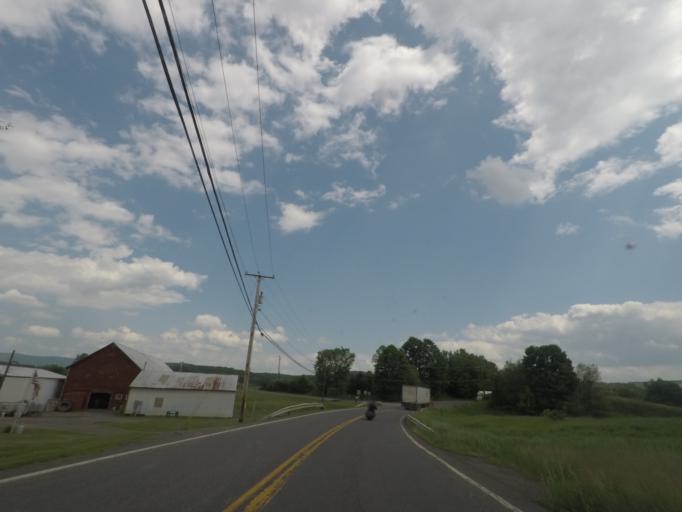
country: US
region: New York
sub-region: Dutchess County
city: Pine Plains
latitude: 42.0451
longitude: -73.6177
